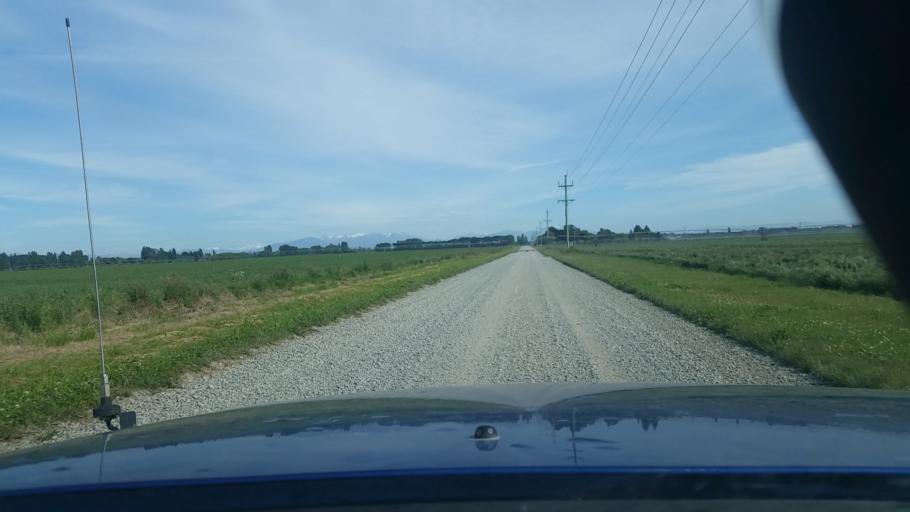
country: NZ
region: Canterbury
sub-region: Ashburton District
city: Tinwald
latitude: -43.9890
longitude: 171.7907
